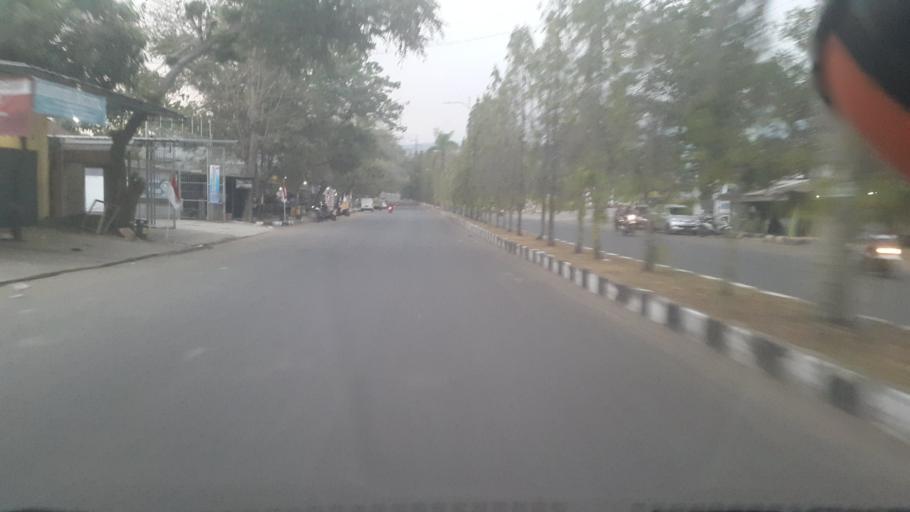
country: ID
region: West Java
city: Pelabuhanratu
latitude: -6.9944
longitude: 106.5579
